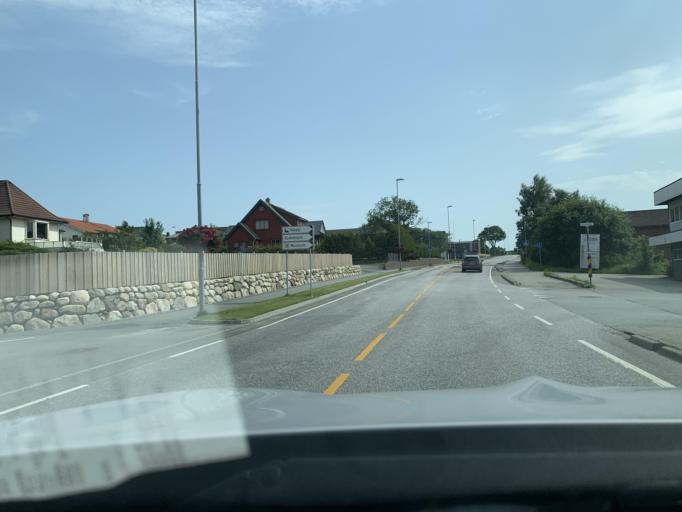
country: NO
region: Rogaland
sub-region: Klepp
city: Kleppe
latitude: 58.7728
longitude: 5.6298
